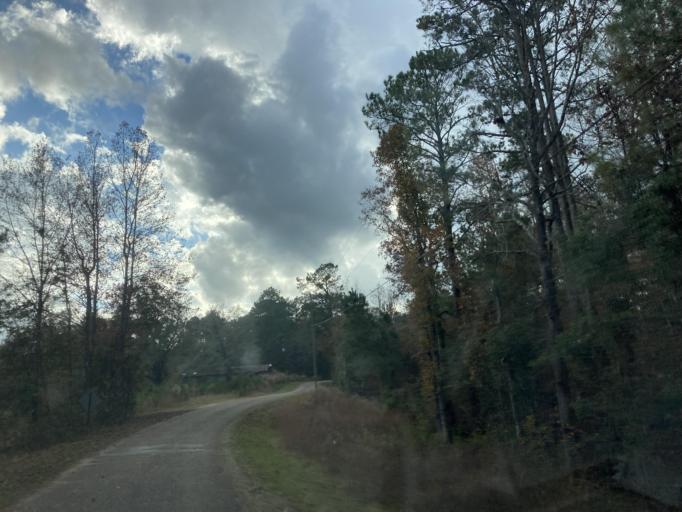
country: US
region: Mississippi
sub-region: Lamar County
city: Purvis
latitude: 31.1639
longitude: -89.6195
